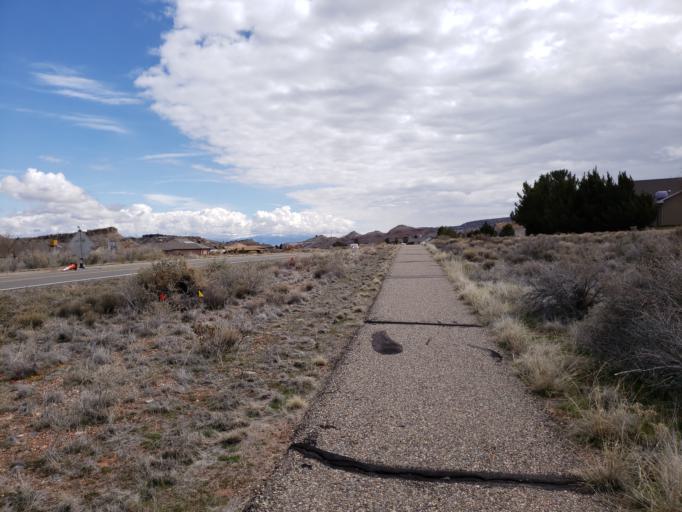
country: US
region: Colorado
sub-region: Mesa County
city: Redlands
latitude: 39.0542
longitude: -108.6434
